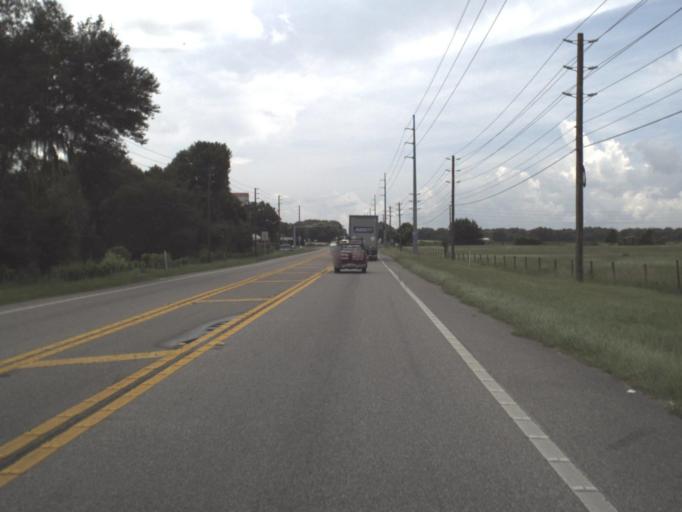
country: US
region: Florida
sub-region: Pasco County
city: San Antonio
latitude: 28.3242
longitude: -82.3610
